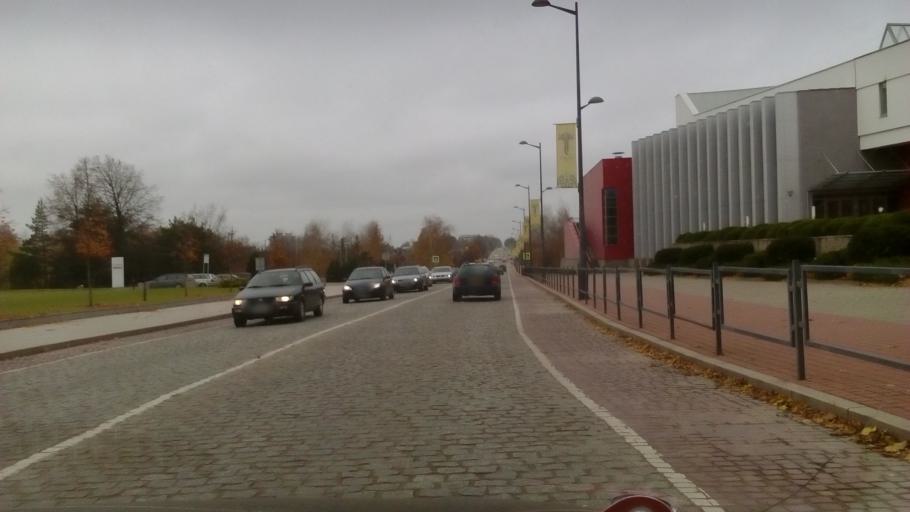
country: LT
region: Marijampoles apskritis
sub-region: Marijampole Municipality
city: Marijampole
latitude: 54.5579
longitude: 23.3498
